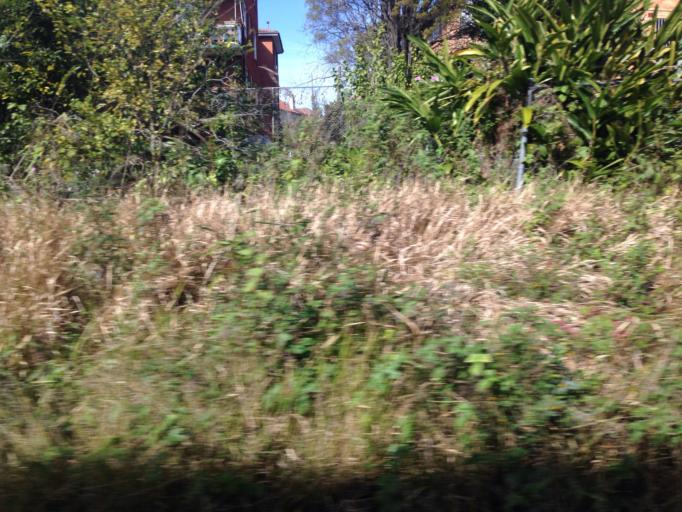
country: AU
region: New South Wales
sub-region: North Sydney
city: Wollstonecraft
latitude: -33.8301
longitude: 151.1928
